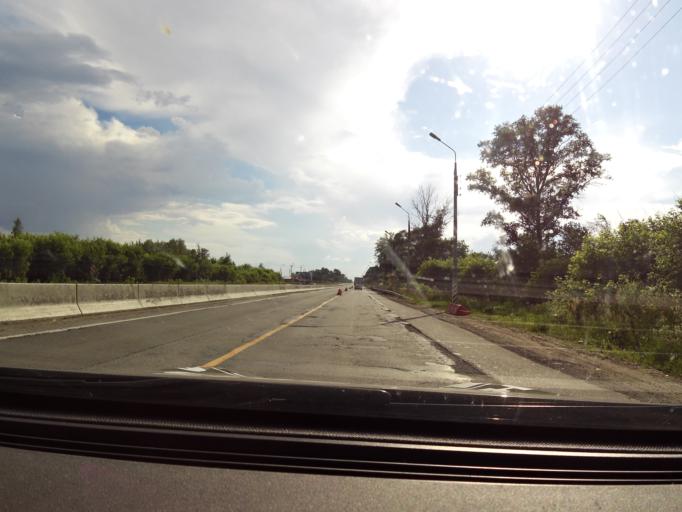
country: RU
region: Nizjnij Novgorod
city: Mulino
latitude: 56.2731
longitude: 42.9610
